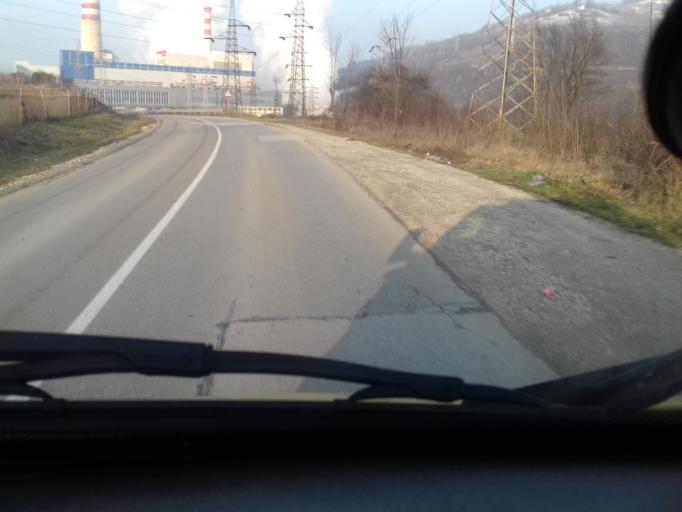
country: BA
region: Federation of Bosnia and Herzegovina
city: Dobrinje
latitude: 44.0829
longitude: 18.1128
